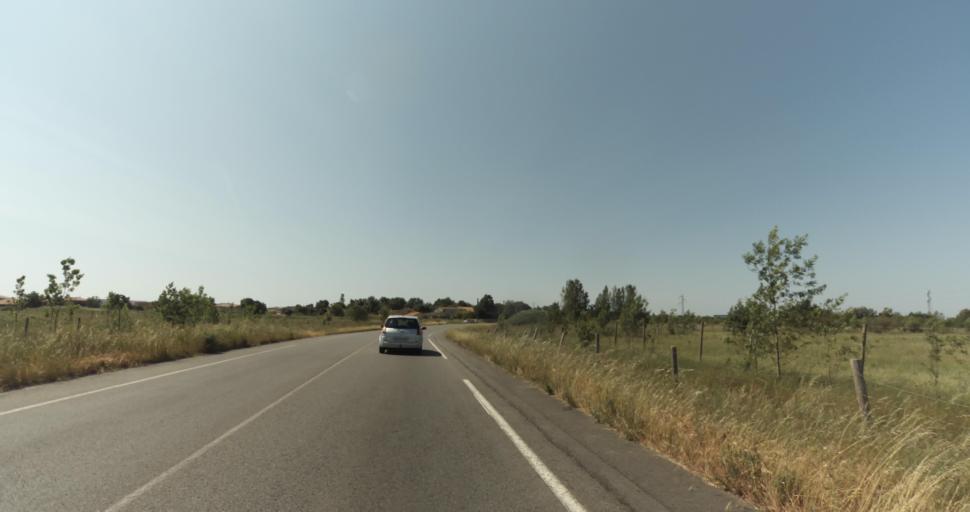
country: FR
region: Midi-Pyrenees
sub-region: Departement de la Haute-Garonne
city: La Salvetat-Saint-Gilles
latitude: 43.5872
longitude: 1.2803
